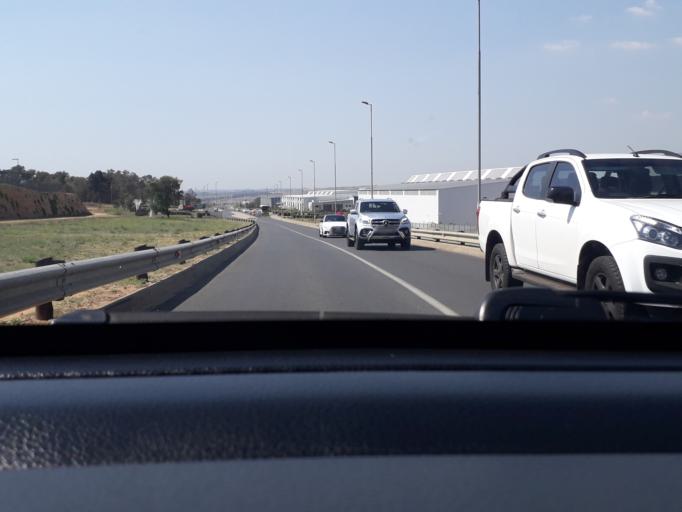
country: ZA
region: Gauteng
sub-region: City of Johannesburg Metropolitan Municipality
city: Modderfontein
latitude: -26.1029
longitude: 28.1386
